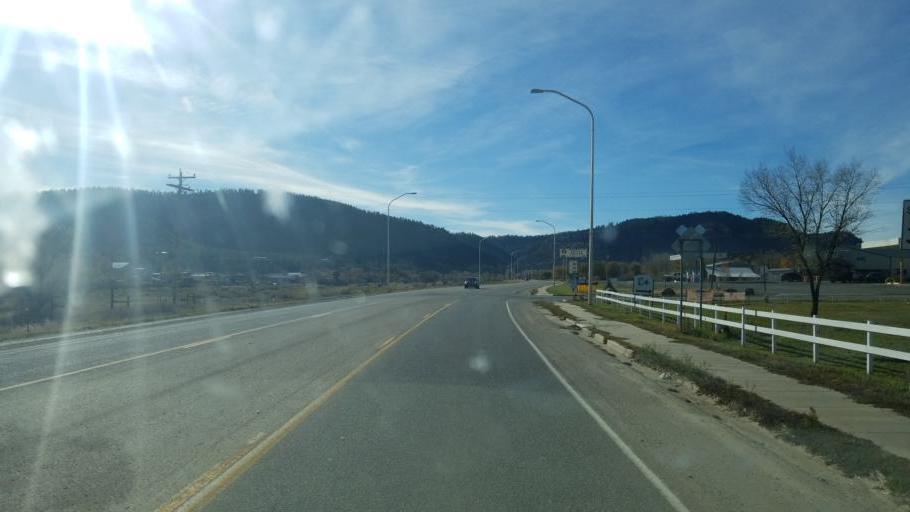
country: US
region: New Mexico
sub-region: Rio Arriba County
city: Dulce
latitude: 36.9337
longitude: -106.9895
